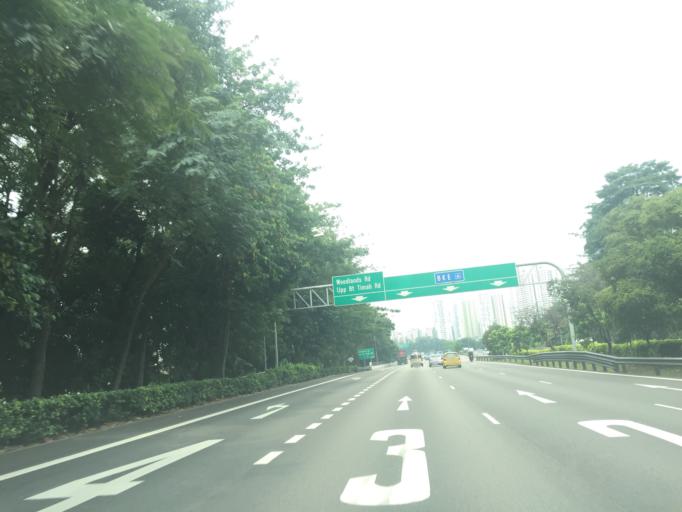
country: MY
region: Johor
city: Johor Bahru
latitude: 1.3896
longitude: 103.7502
